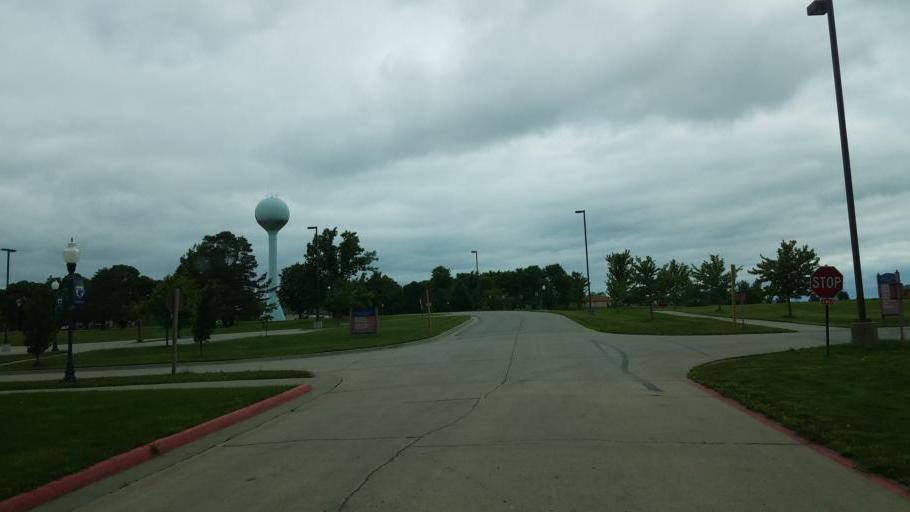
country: US
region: Iowa
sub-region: Decatur County
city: Lamoni
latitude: 40.6161
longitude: -93.9230
